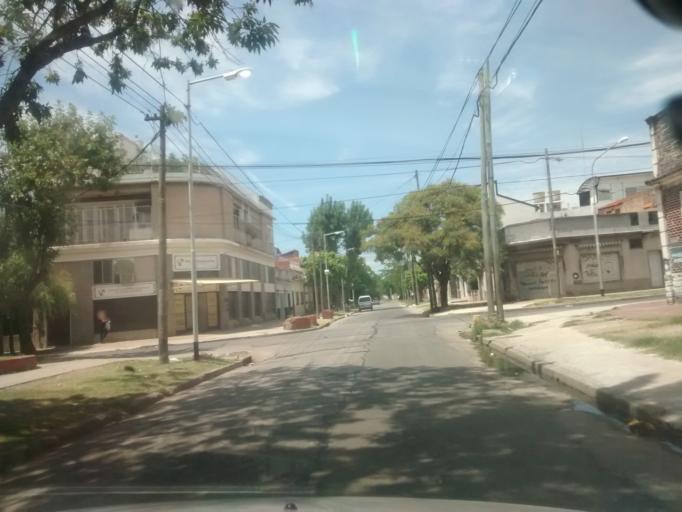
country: AR
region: Buenos Aires
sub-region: Partido de Avellaneda
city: Avellaneda
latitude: -34.6824
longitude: -58.3510
